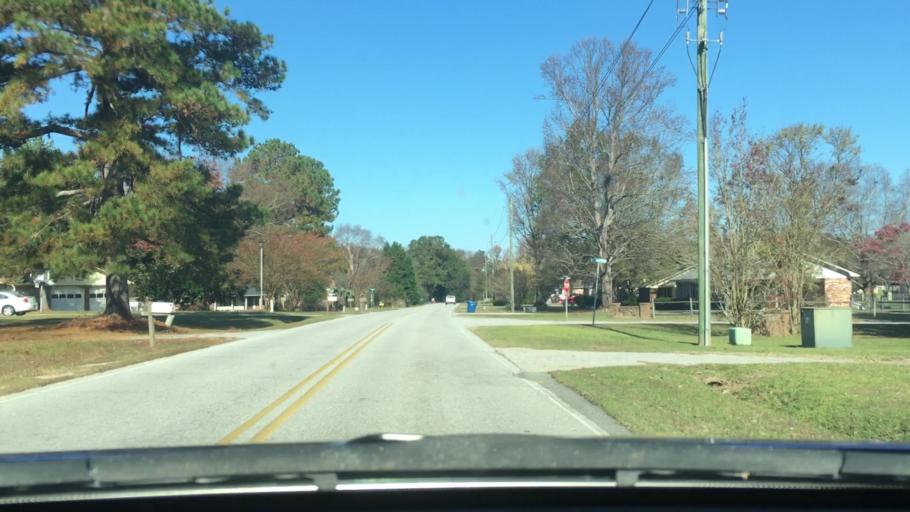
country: US
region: South Carolina
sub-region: Sumter County
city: Cane Savannah
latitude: 33.8977
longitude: -80.4079
